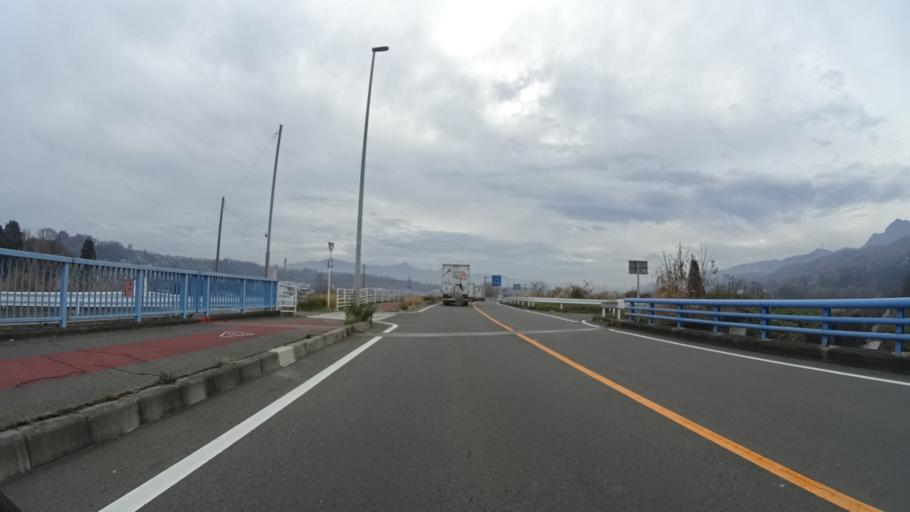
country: JP
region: Gunma
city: Numata
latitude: 36.6484
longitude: 139.0266
